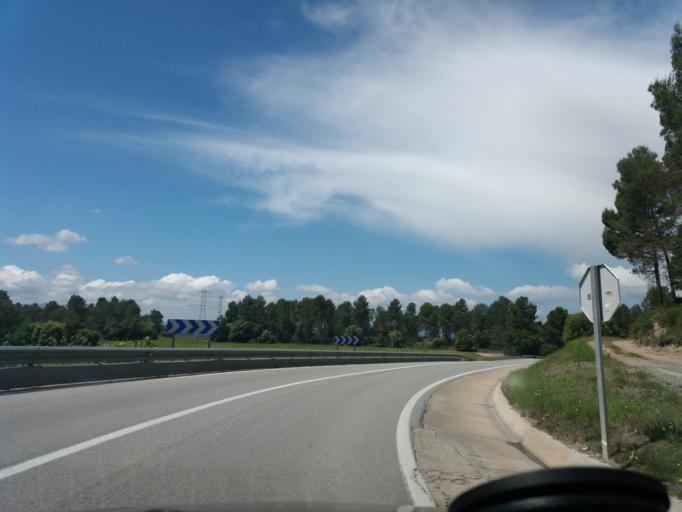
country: ES
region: Catalonia
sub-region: Provincia de Barcelona
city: Artes
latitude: 41.7702
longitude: 1.9473
